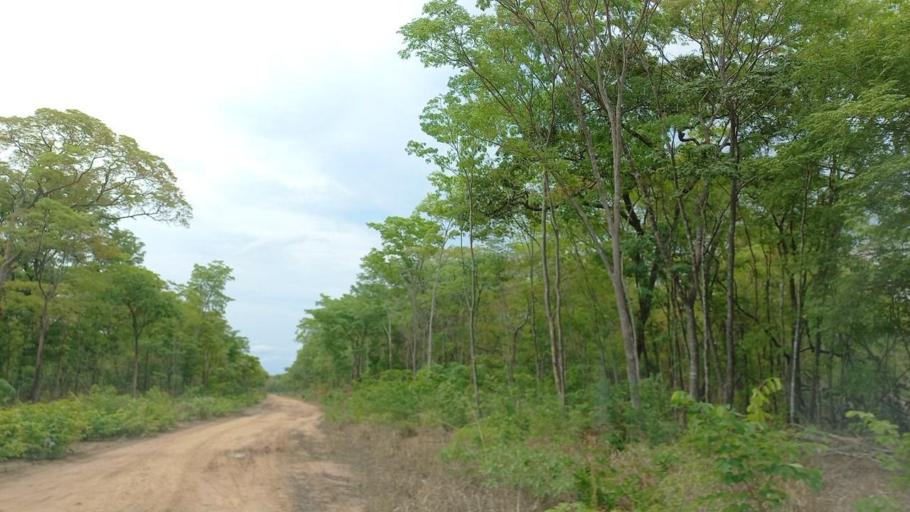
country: ZM
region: North-Western
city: Kalengwa
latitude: -13.5650
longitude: 24.9714
